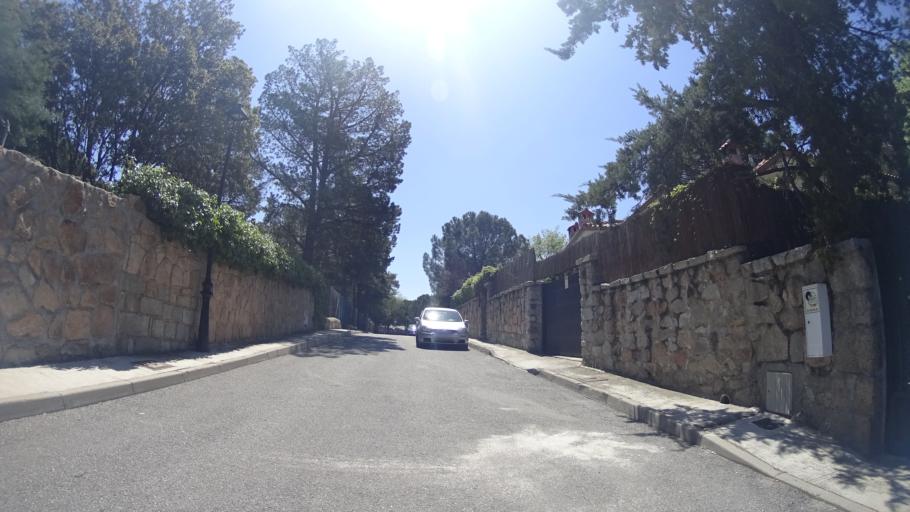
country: ES
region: Madrid
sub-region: Provincia de Madrid
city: Galapagar
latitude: 40.5854
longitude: -3.9698
